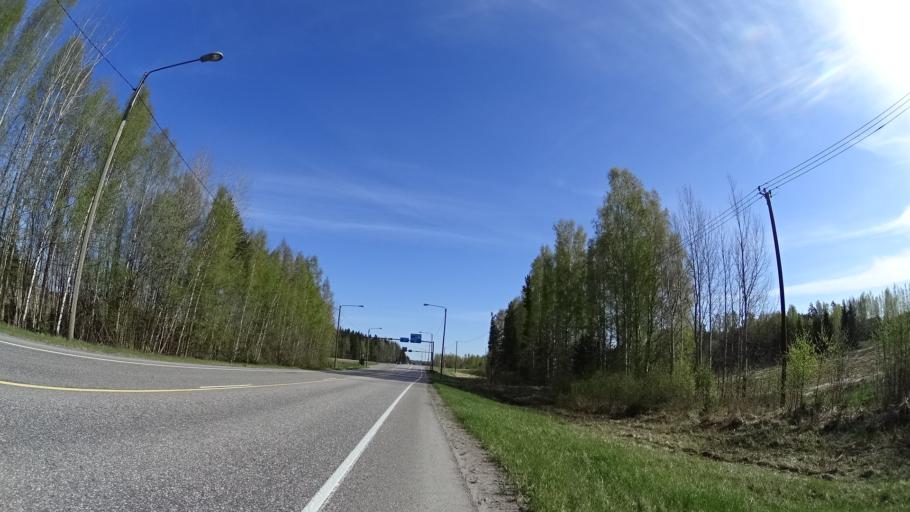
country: FI
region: Uusimaa
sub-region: Helsinki
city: Nurmijaervi
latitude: 60.3941
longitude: 24.8118
